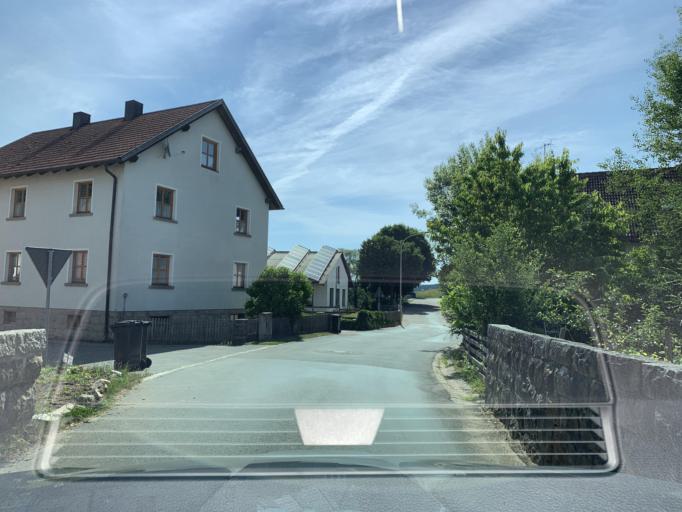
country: DE
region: Bavaria
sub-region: Upper Palatinate
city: Altendorf
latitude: 49.3976
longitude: 12.3090
